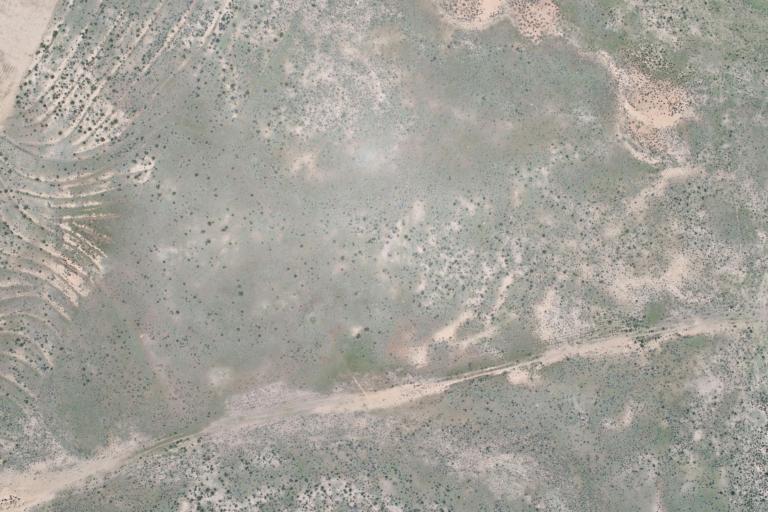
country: BO
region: La Paz
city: Patacamaya
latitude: -17.2732
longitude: -68.5088
